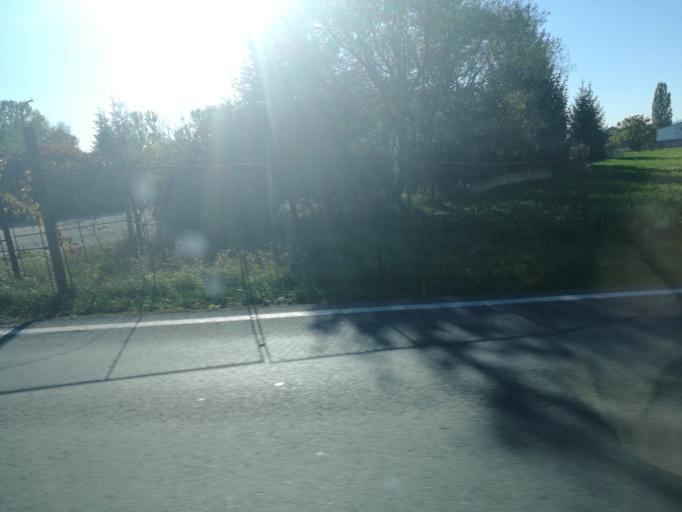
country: RO
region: Brasov
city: Brasov
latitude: 45.6812
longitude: 25.5853
